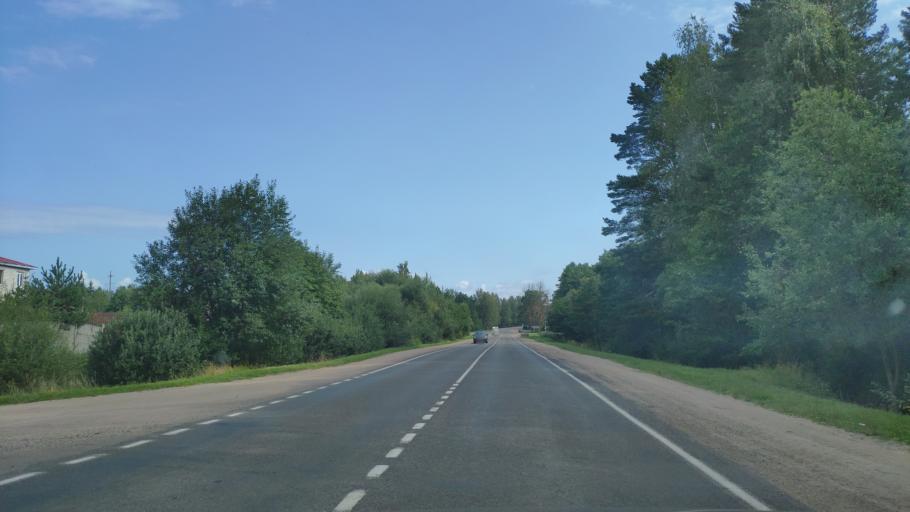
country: BY
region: Minsk
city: Zaslawye
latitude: 53.9838
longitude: 27.2554
